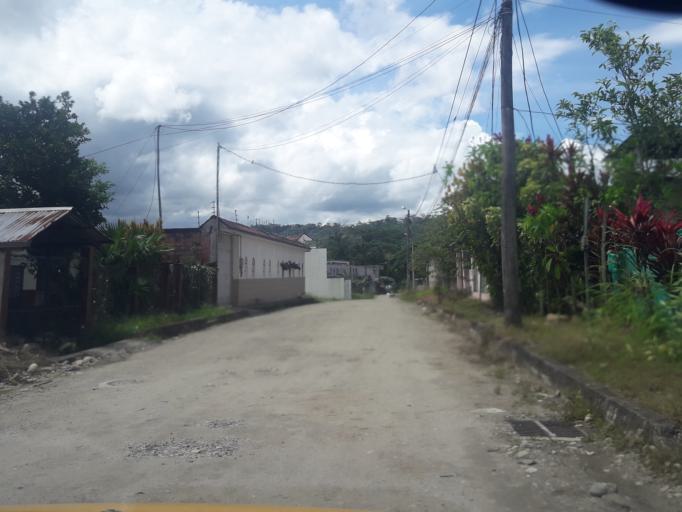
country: EC
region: Napo
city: Tena
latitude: -1.0032
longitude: -77.8190
